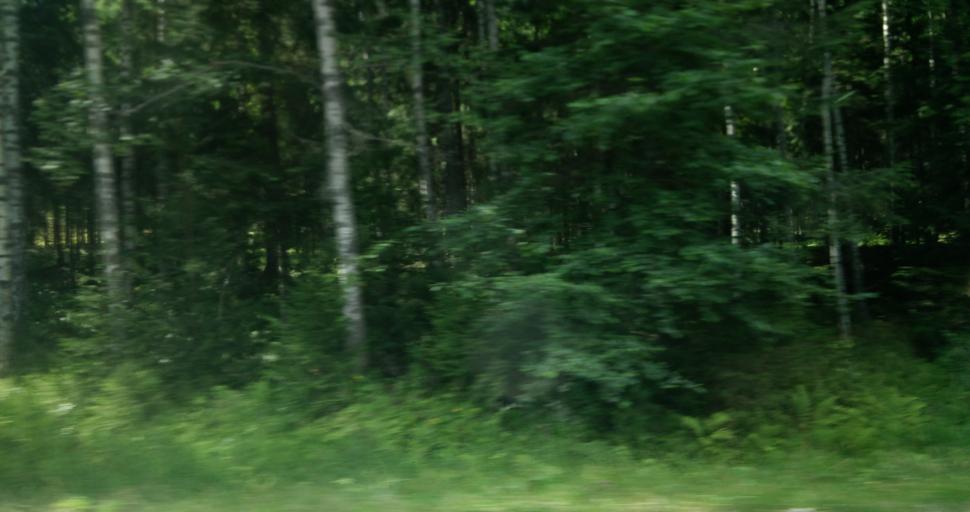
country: SE
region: Vaermland
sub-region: Hagfors Kommun
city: Ekshaerad
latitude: 60.0773
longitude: 13.4630
